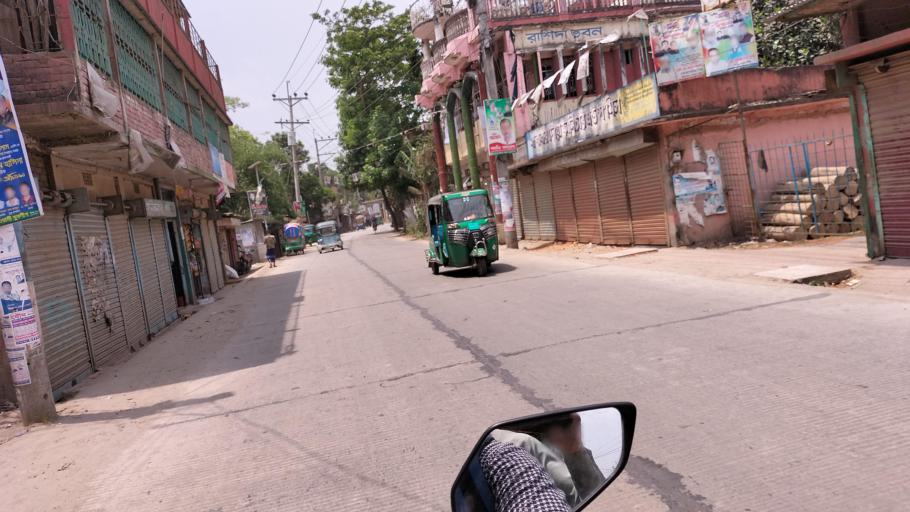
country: BD
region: Dhaka
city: Azimpur
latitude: 23.7334
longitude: 90.2703
